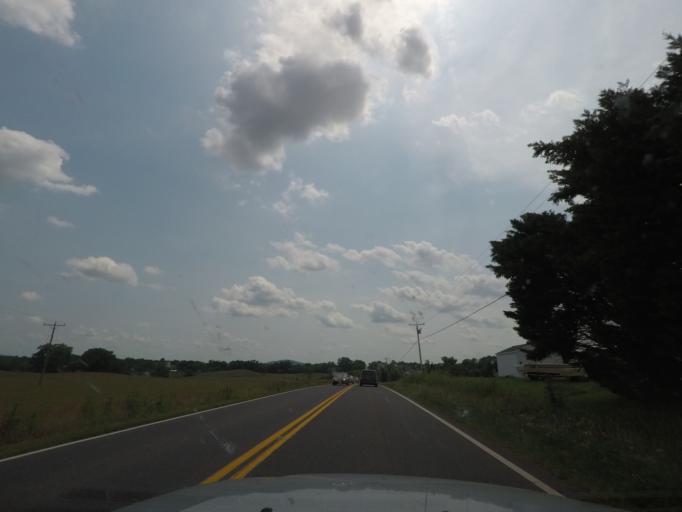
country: US
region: Virginia
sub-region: Culpeper County
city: Culpeper
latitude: 38.4357
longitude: -78.0270
